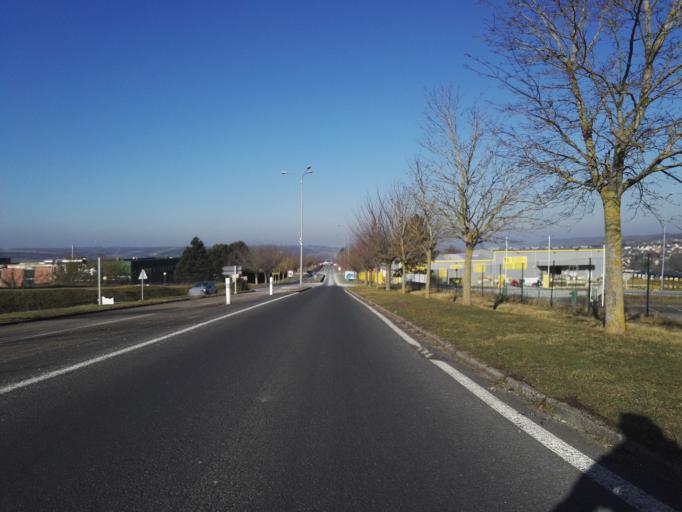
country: FR
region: Haute-Normandie
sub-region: Departement de l'Eure
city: Pacy-sur-Eure
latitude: 49.0091
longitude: 1.4020
